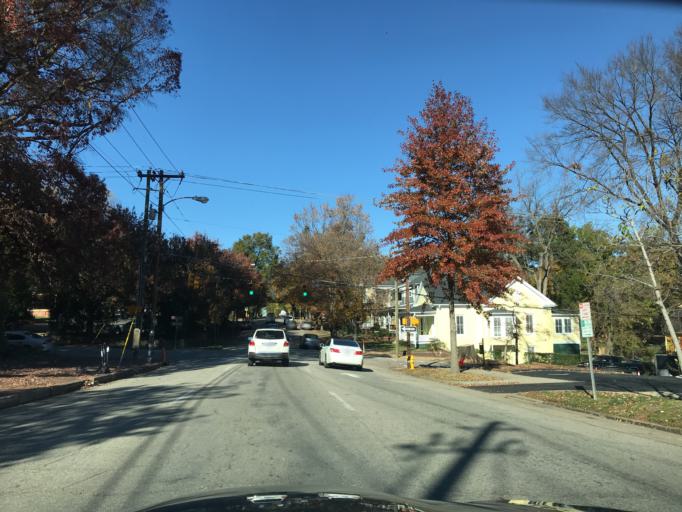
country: US
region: North Carolina
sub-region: Wake County
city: Raleigh
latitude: 35.7833
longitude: -78.6347
